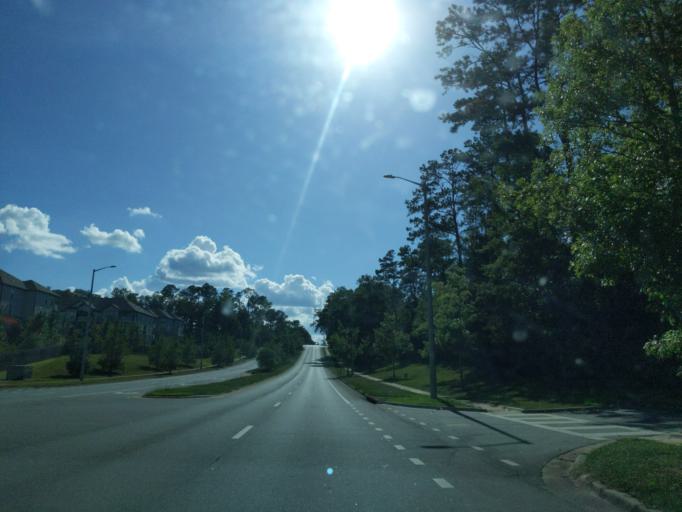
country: US
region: Florida
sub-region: Leon County
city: Tallahassee
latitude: 30.4107
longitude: -84.2407
